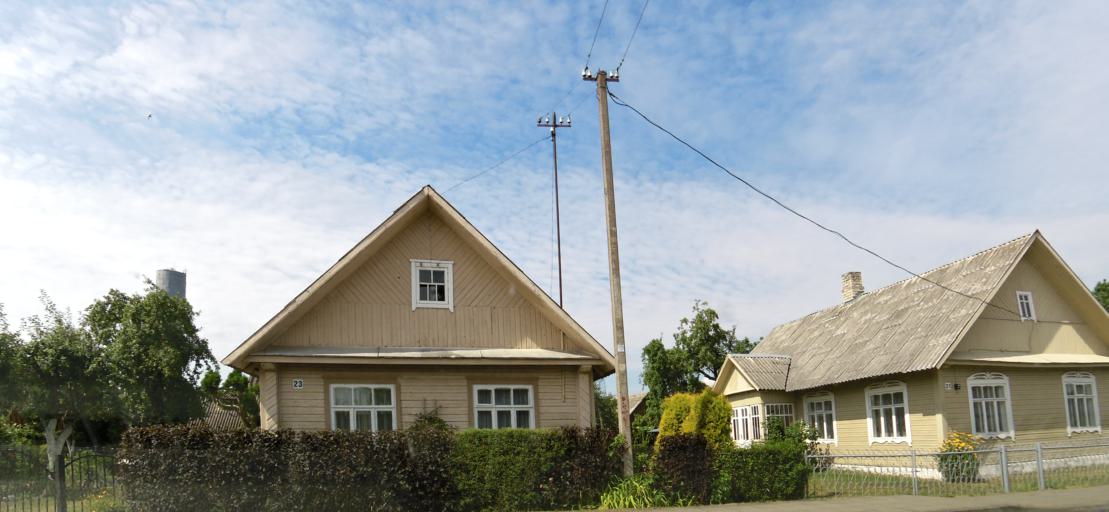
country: LT
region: Vilnius County
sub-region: Trakai
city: Rudiskes
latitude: 54.3609
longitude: 24.8402
